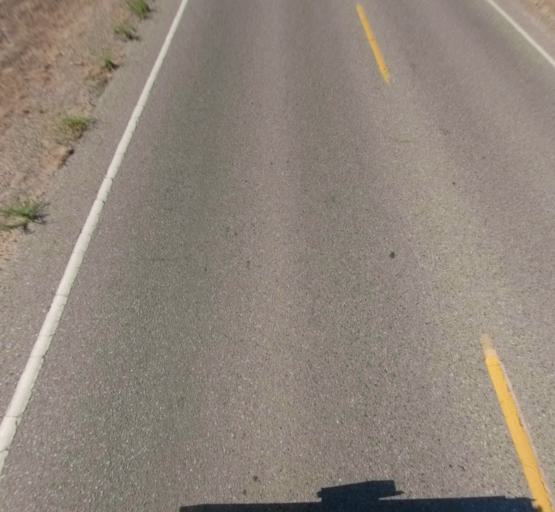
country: US
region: California
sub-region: Madera County
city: Madera Acres
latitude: 36.9863
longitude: -120.1285
